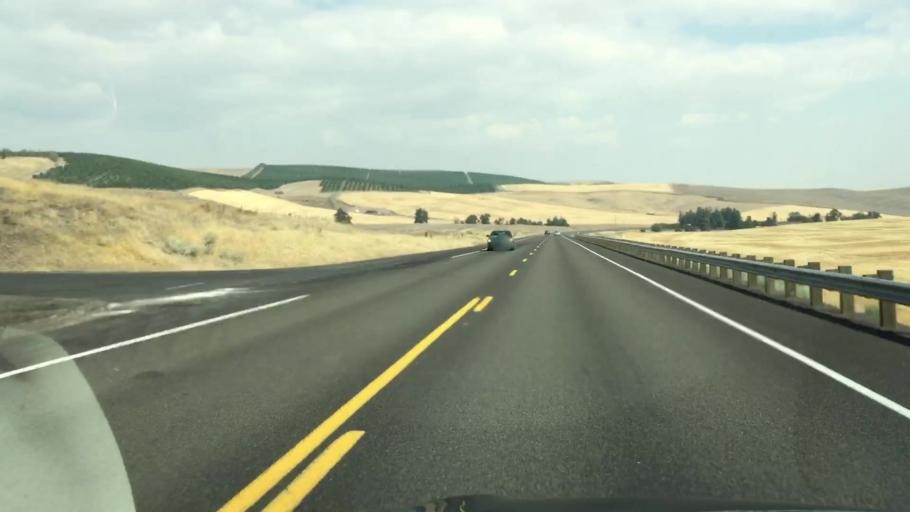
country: US
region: Oregon
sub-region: Wasco County
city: The Dalles
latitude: 45.4776
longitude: -121.1174
